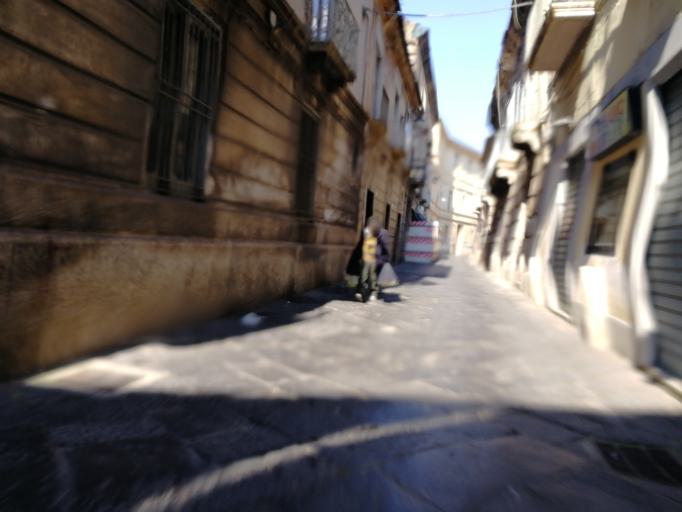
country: IT
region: Campania
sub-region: Provincia di Caserta
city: Santa Maria Capua Vetere
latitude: 41.0789
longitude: 14.2569
